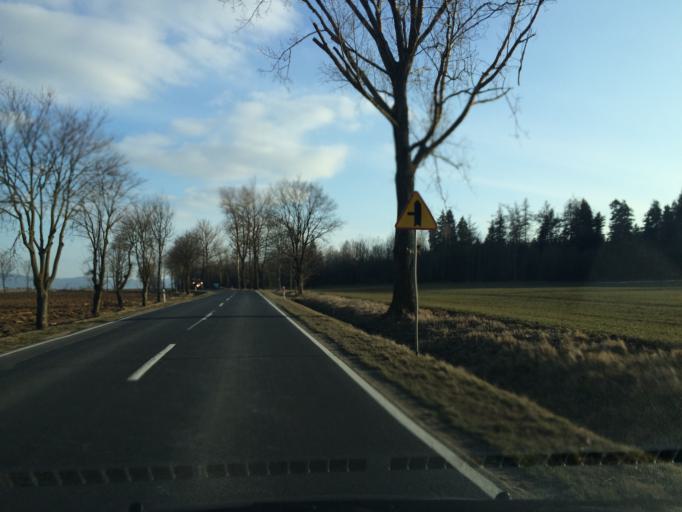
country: PL
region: Lower Silesian Voivodeship
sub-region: Powiat klodzki
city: Bystrzyca Klodzka
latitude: 50.2395
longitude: 16.6739
